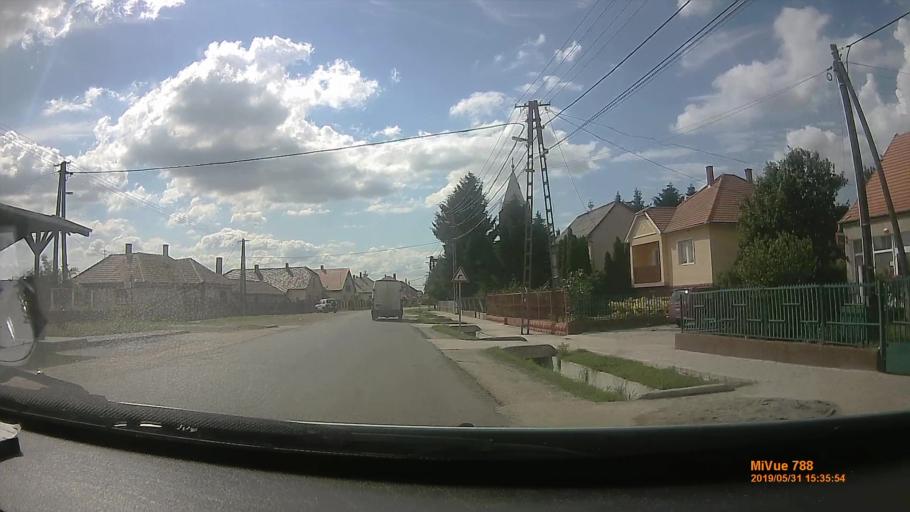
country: HU
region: Borsod-Abauj-Zemplen
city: Prugy
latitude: 48.0813
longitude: 21.2414
